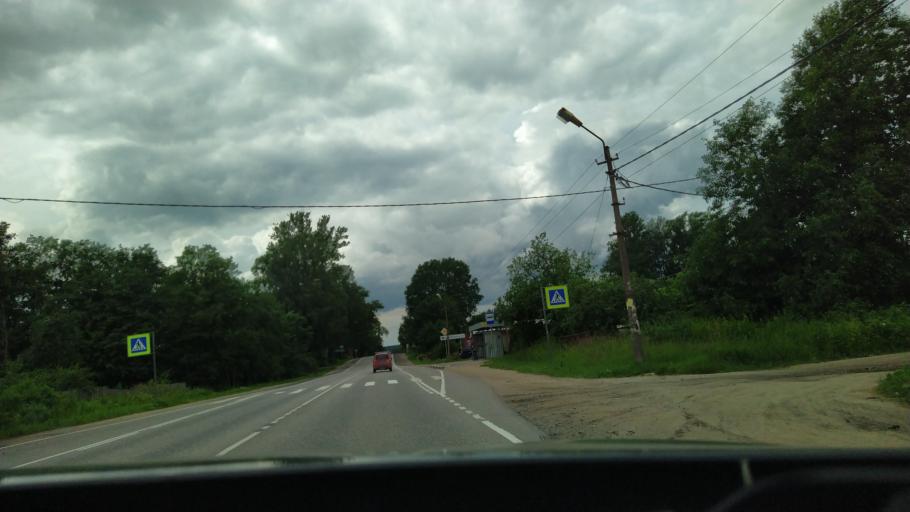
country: RU
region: Leningrad
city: Pavlovo
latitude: 59.8104
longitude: 30.9062
